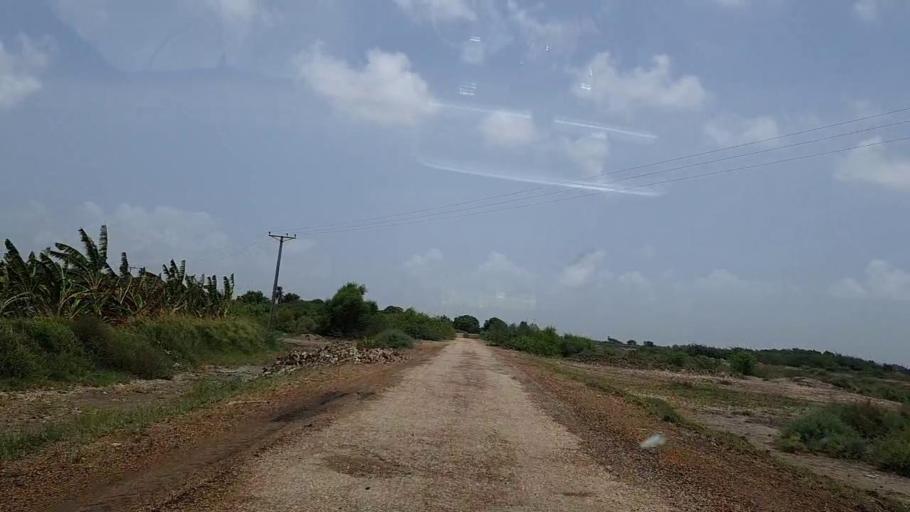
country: PK
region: Sindh
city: Keti Bandar
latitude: 24.1668
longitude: 67.5436
